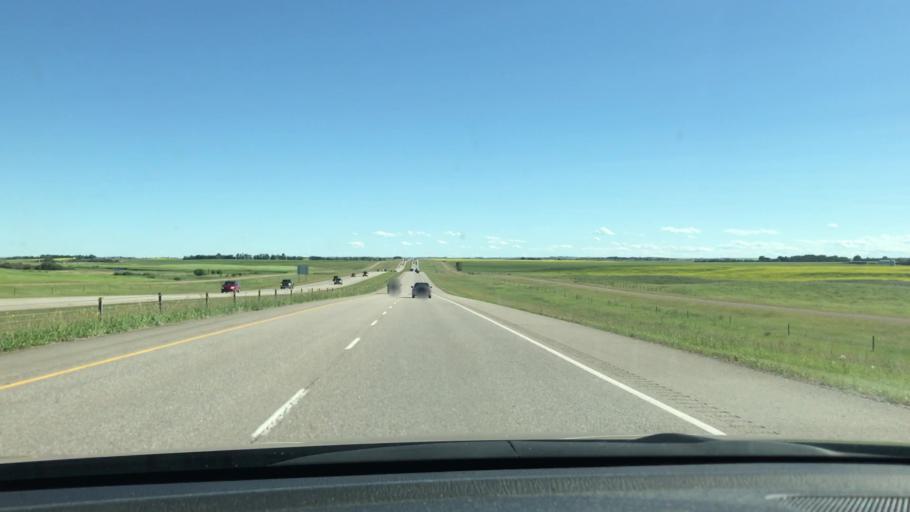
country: CA
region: Alberta
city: Carstairs
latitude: 51.6451
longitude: -114.0257
